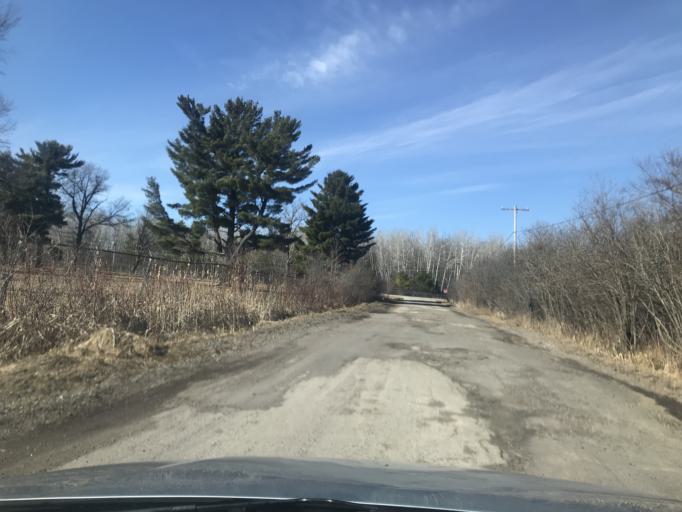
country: US
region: Wisconsin
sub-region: Marinette County
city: Marinette
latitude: 45.1141
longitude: -87.6509
